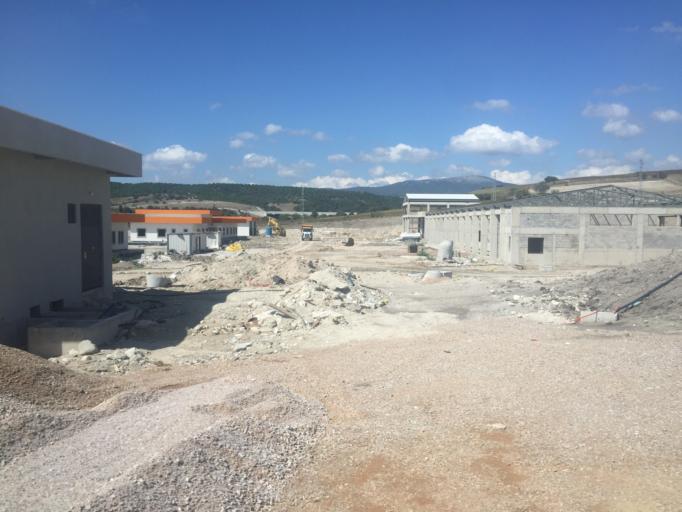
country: TR
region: Balikesir
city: Susurluk
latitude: 39.9616
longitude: 28.1648
